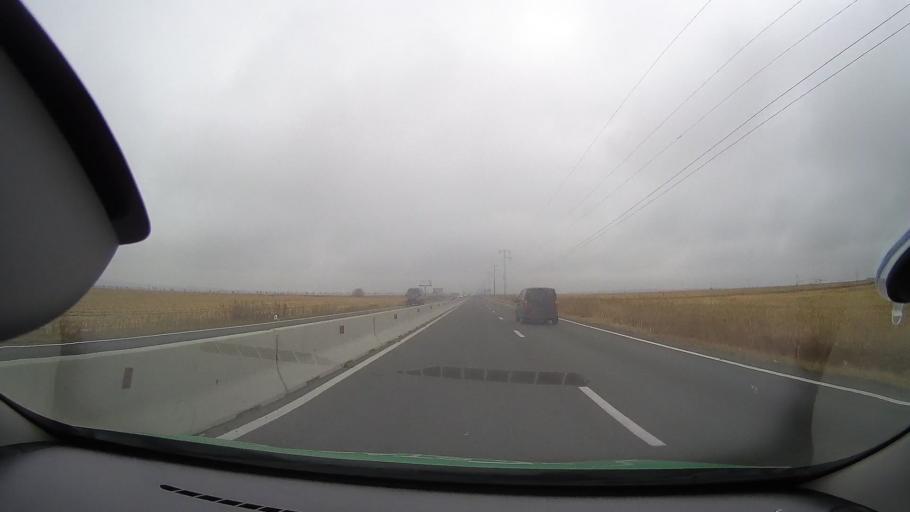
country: RO
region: Prahova
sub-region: Oras Baicoi
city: Baicoi
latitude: 45.0099
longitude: 25.8676
